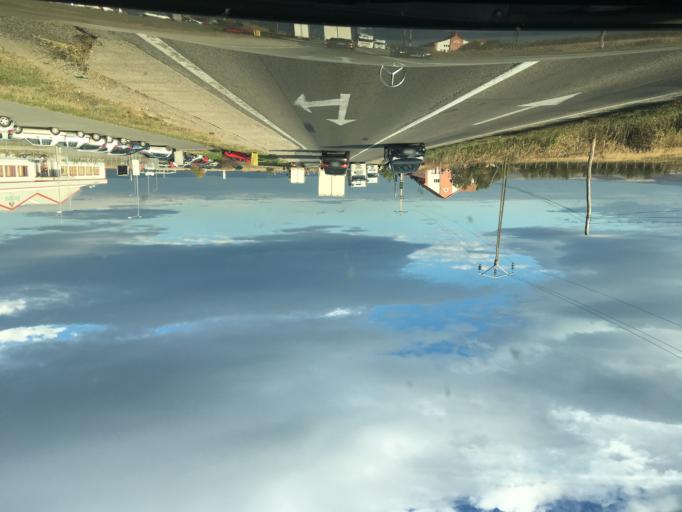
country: RO
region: Alba
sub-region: Comuna Santimbru
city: Santimbru
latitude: 46.1634
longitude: 23.6468
